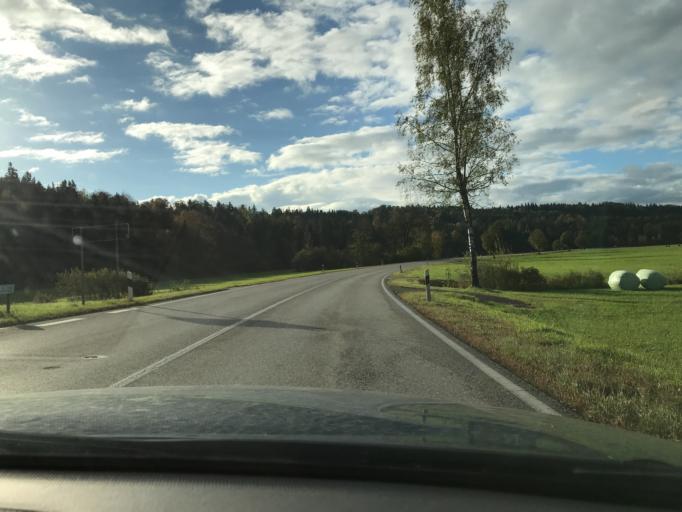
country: DE
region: Bavaria
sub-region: Upper Bavaria
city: Bad Toelz
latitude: 47.8092
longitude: 11.5562
